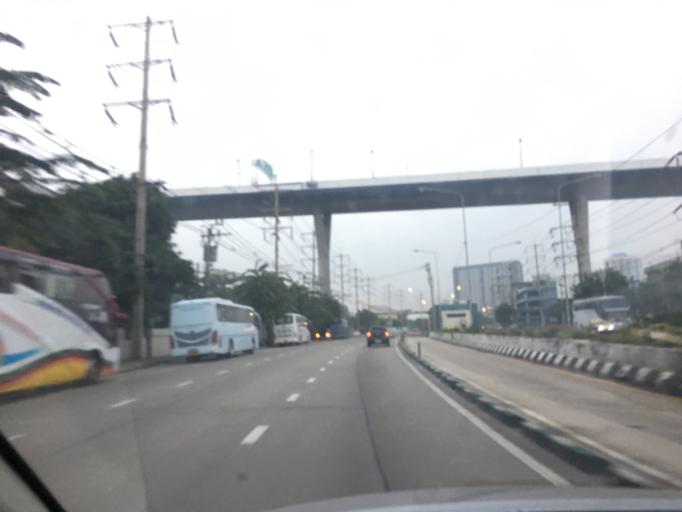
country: TH
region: Samut Prakan
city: Phra Pradaeng
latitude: 13.6730
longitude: 100.5404
